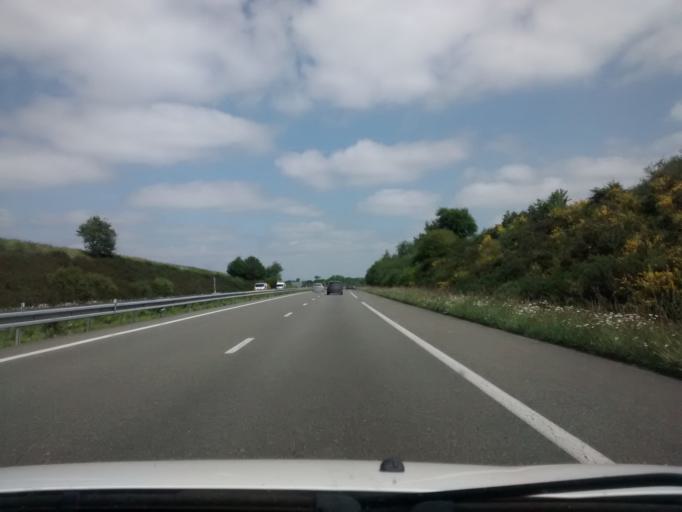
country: FR
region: Pays de la Loire
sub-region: Departement de la Mayenne
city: Saint-Berthevin
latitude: 48.1005
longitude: -0.8476
